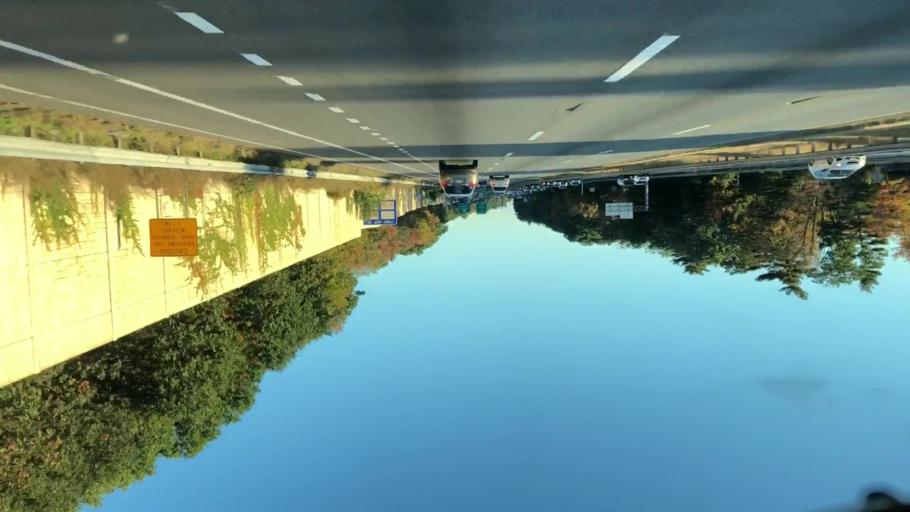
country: US
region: Massachusetts
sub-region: Essex County
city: Andover
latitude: 42.6267
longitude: -71.1782
